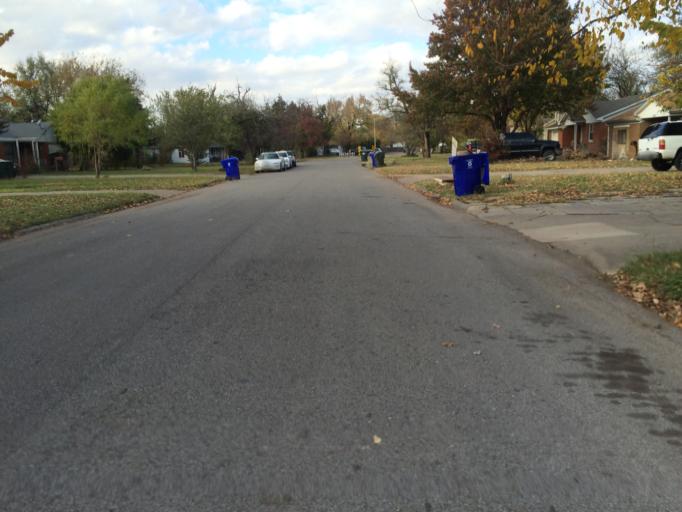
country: US
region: Oklahoma
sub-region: Cleveland County
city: Norman
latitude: 35.2371
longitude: -97.4518
